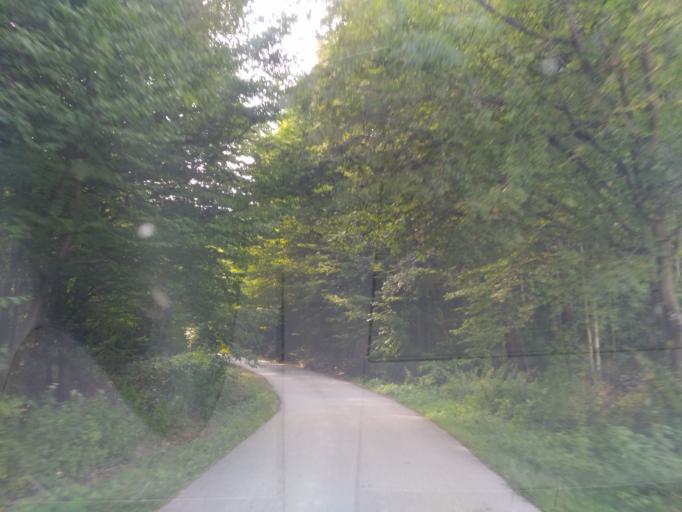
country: SK
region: Kosicky
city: Kosice
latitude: 48.7315
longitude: 21.1795
